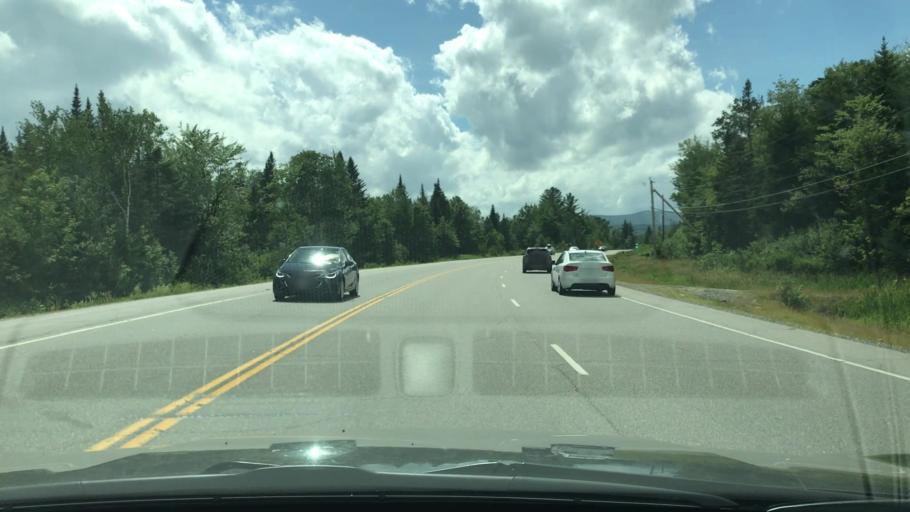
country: US
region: New Hampshire
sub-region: Coos County
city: Jefferson
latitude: 44.3585
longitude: -71.3415
